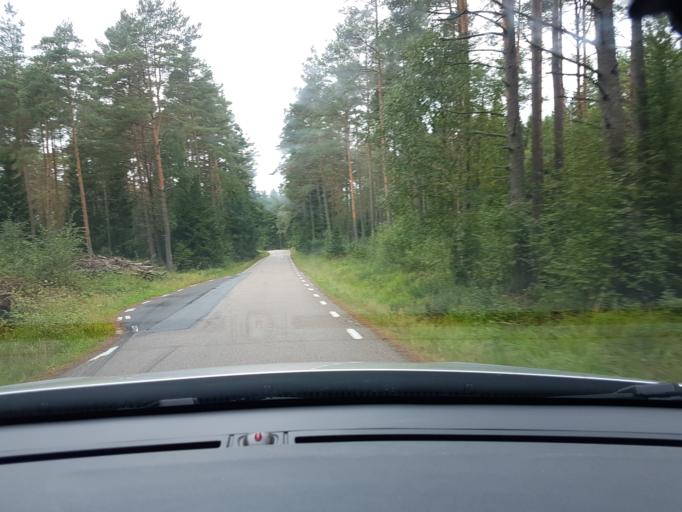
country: SE
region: Vaestra Goetaland
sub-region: Ale Kommun
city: Alvangen
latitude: 57.9074
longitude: 12.1701
